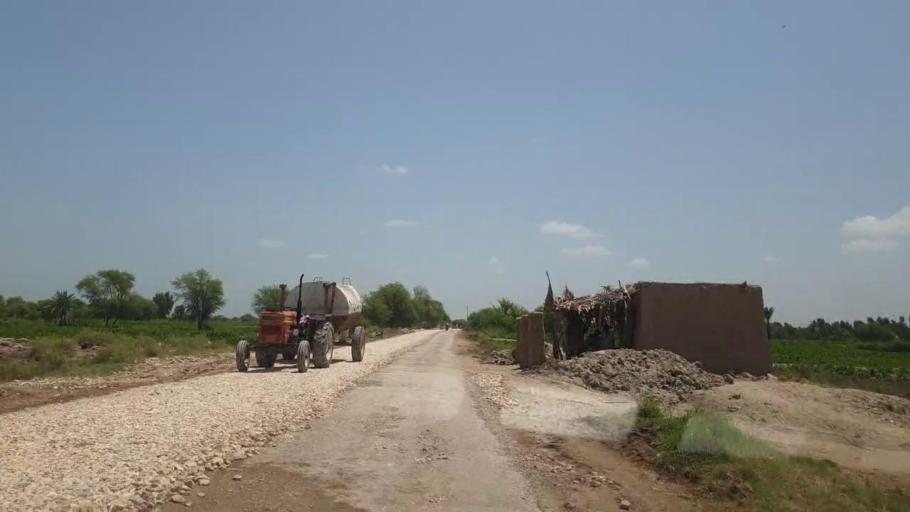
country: PK
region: Sindh
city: Pano Aqil
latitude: 27.6661
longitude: 69.1806
